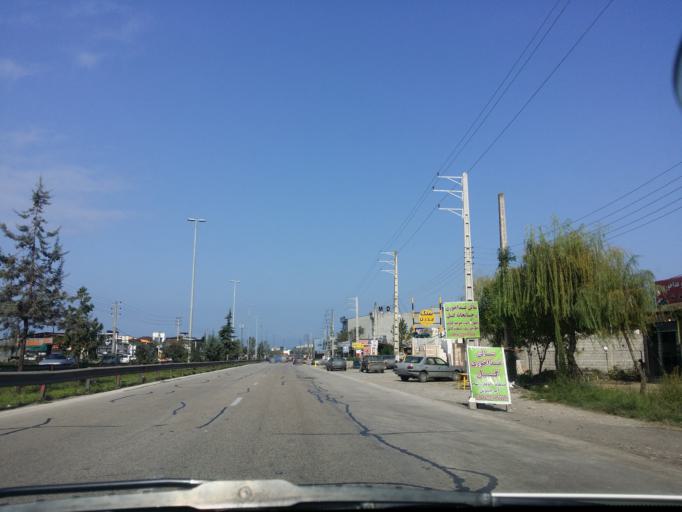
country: IR
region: Mazandaran
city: Chalus
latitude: 36.6670
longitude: 51.3969
